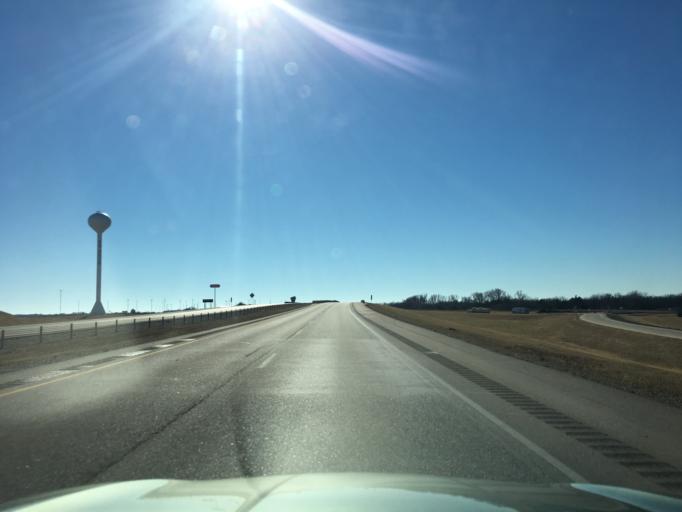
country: US
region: Oklahoma
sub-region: Kay County
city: Blackwell
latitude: 36.9441
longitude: -97.3461
